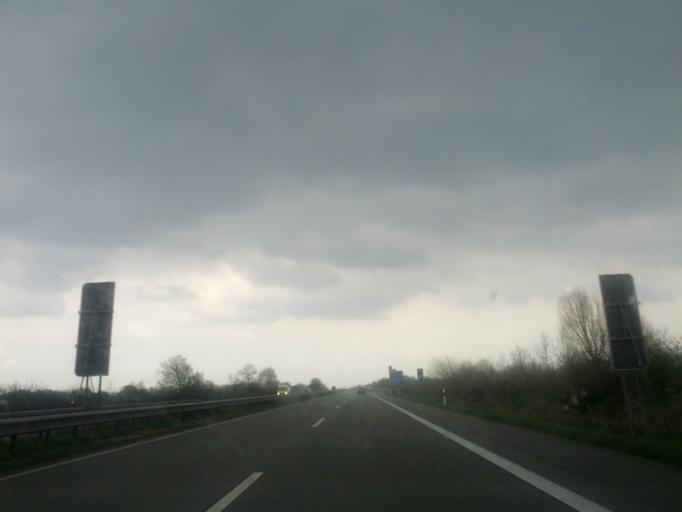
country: DE
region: Lower Saxony
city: Filsum
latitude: 53.2514
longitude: 7.6263
